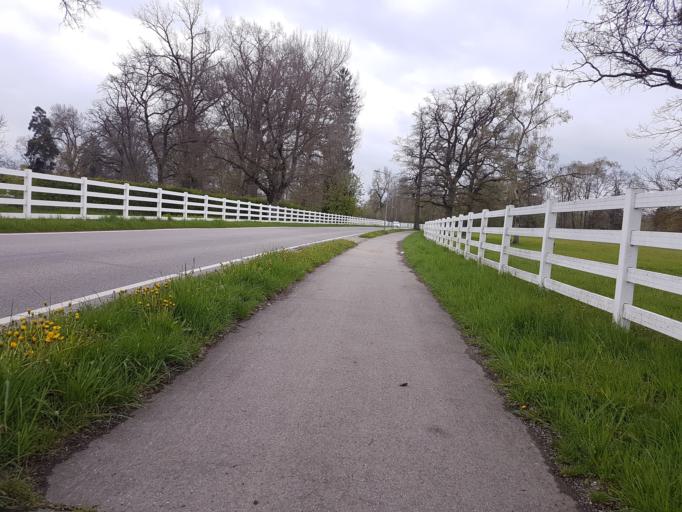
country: DE
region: Baden-Wuerttemberg
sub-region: Freiburg Region
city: Donaueschingen
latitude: 47.9534
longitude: 8.5118
